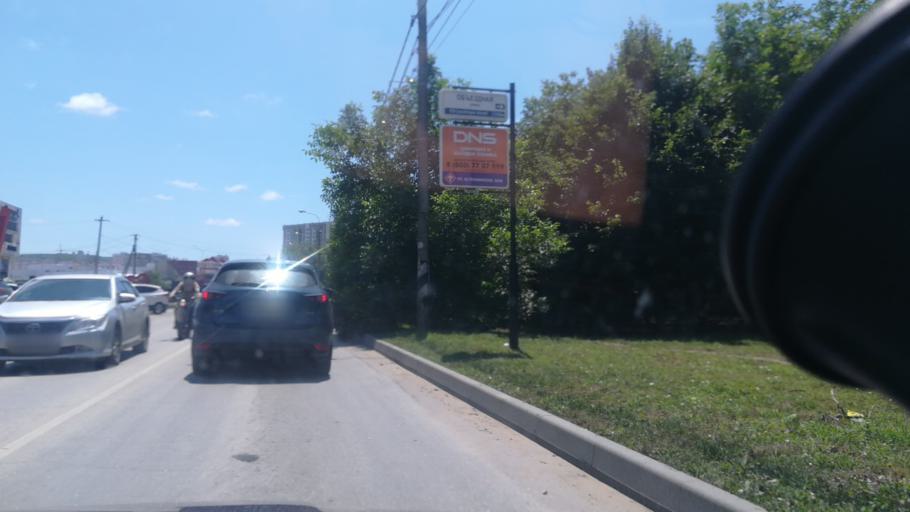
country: RU
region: Krasnodarskiy
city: Anapa
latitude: 44.8840
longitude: 37.3381
